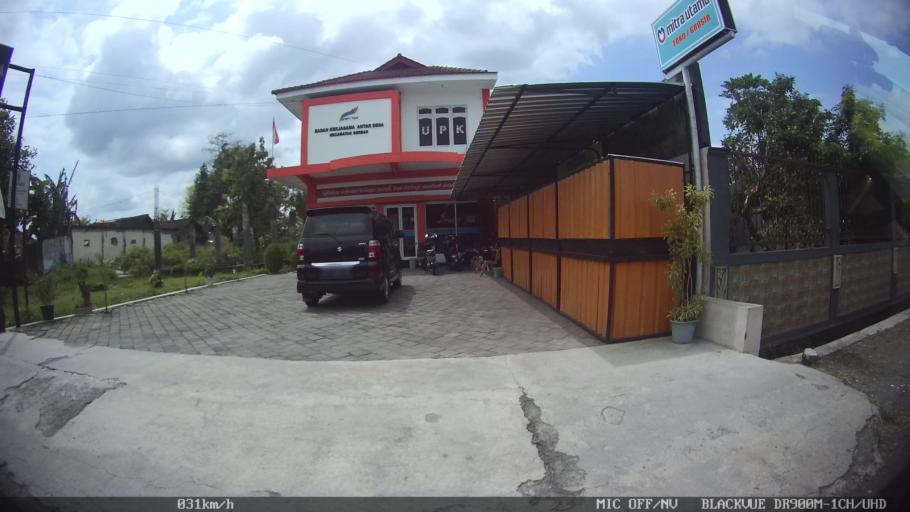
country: ID
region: Daerah Istimewa Yogyakarta
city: Depok
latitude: -7.8182
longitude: 110.4428
